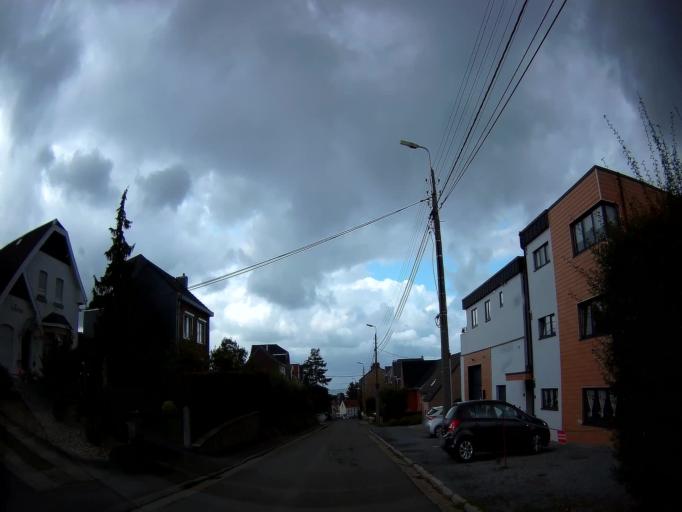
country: BE
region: Wallonia
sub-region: Province de Liege
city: Verviers
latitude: 50.5920
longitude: 5.8994
